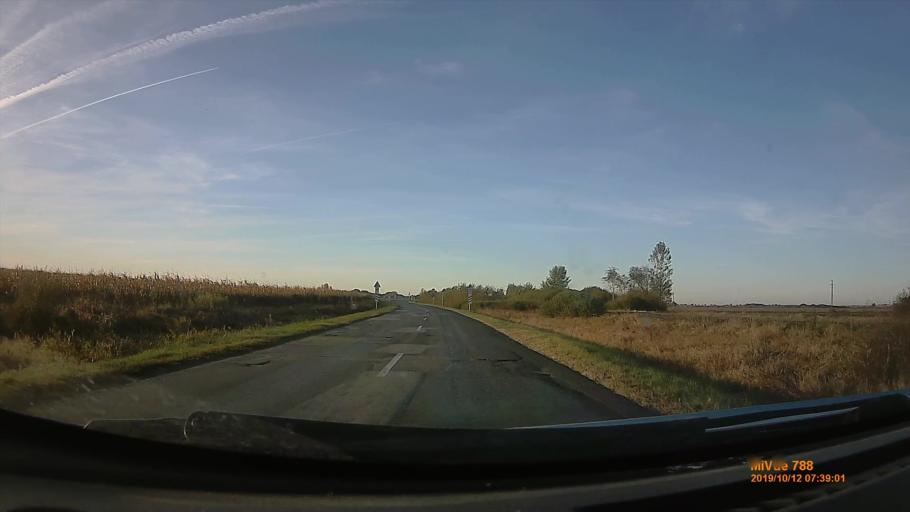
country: HU
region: Hajdu-Bihar
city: Pocsaj
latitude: 47.2185
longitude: 21.8057
